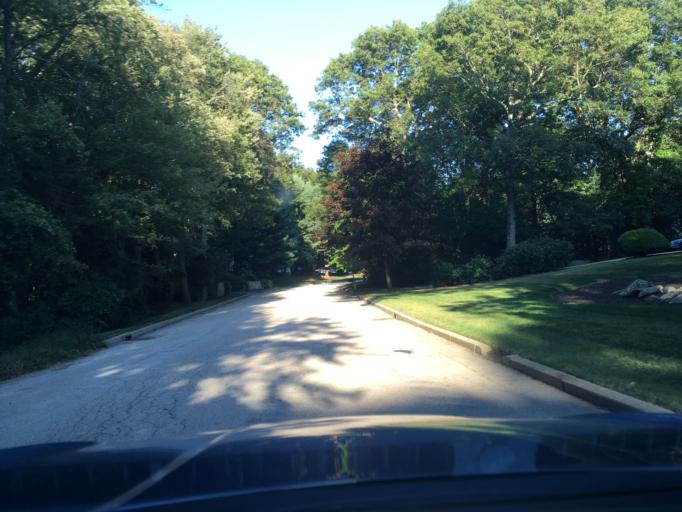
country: US
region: Rhode Island
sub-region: Kent County
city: West Warwick
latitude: 41.6492
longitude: -71.5163
